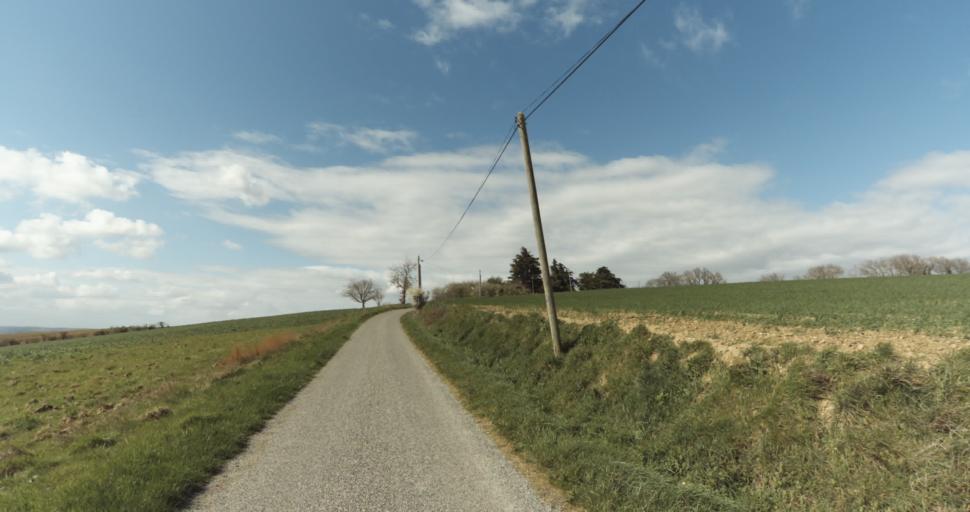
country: FR
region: Midi-Pyrenees
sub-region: Departement de la Haute-Garonne
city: Auterive
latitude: 43.3745
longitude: 1.5027
